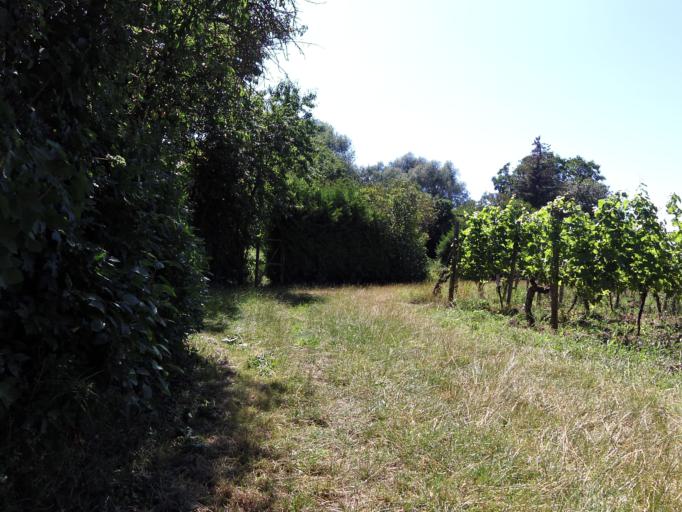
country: DE
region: Bavaria
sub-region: Regierungsbezirk Unterfranken
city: Randersacker
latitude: 49.7645
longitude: 9.9658
